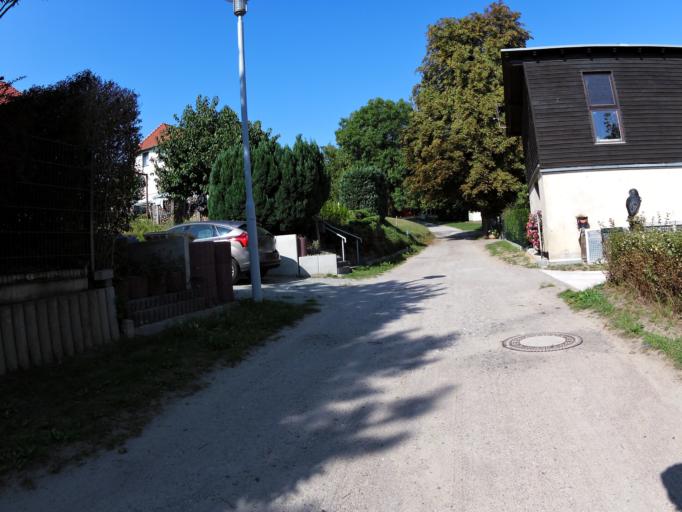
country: DE
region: Mecklenburg-Vorpommern
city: Seebad Bansin
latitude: 53.9683
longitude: 14.0710
